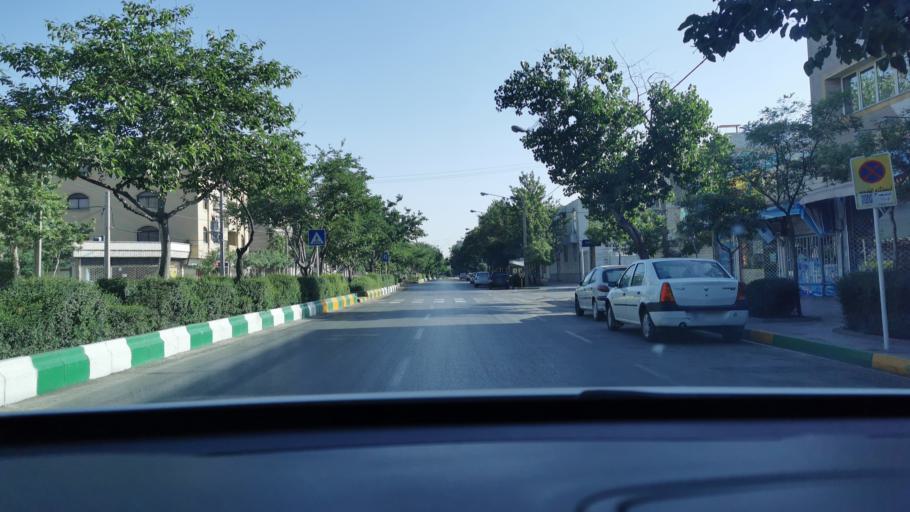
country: IR
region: Razavi Khorasan
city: Mashhad
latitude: 36.3346
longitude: 59.5123
